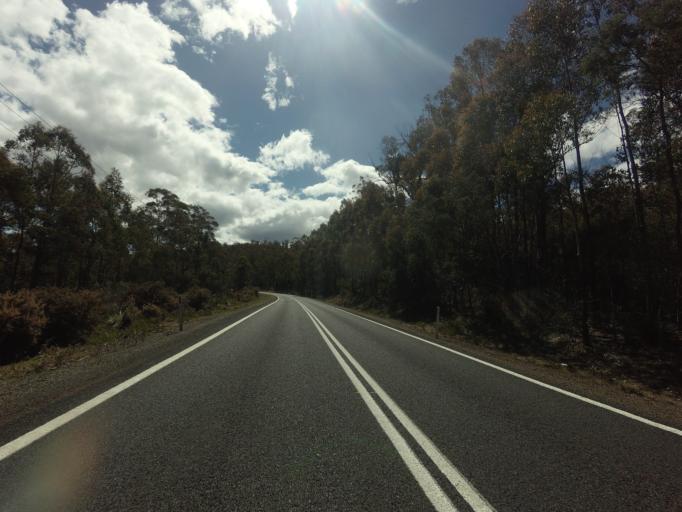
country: AU
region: Tasmania
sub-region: Northern Midlands
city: Evandale
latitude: -42.0337
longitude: 147.8127
